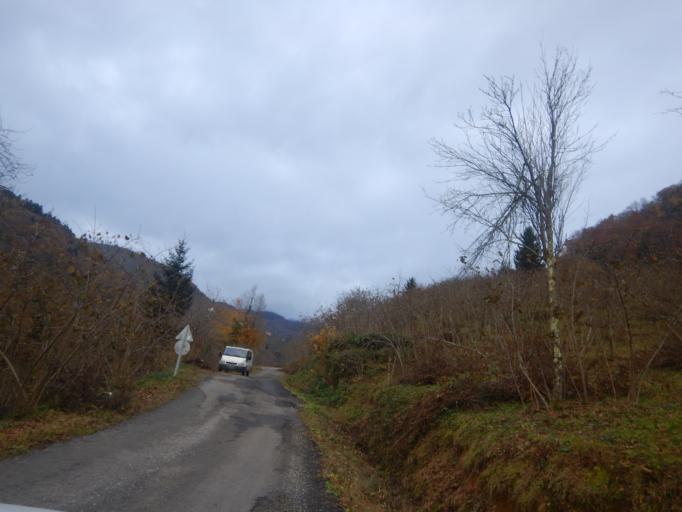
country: TR
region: Ordu
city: Kabaduz
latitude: 40.8727
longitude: 37.9191
